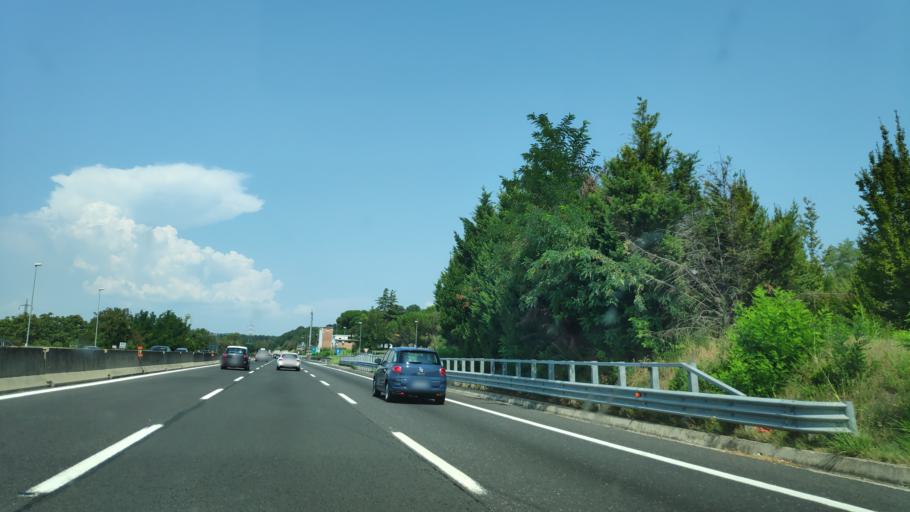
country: IT
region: Latium
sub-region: Provincia di Rieti
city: Magliano Sabina
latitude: 42.3809
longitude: 12.4715
